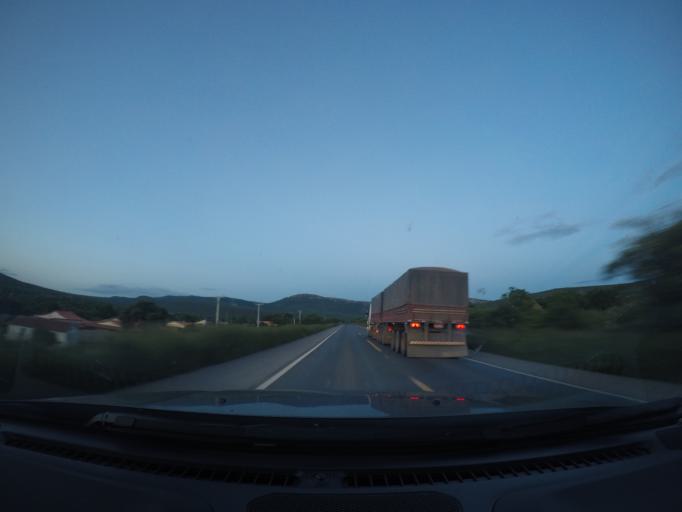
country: BR
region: Bahia
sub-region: Seabra
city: Seabra
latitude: -12.4805
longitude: -41.7188
